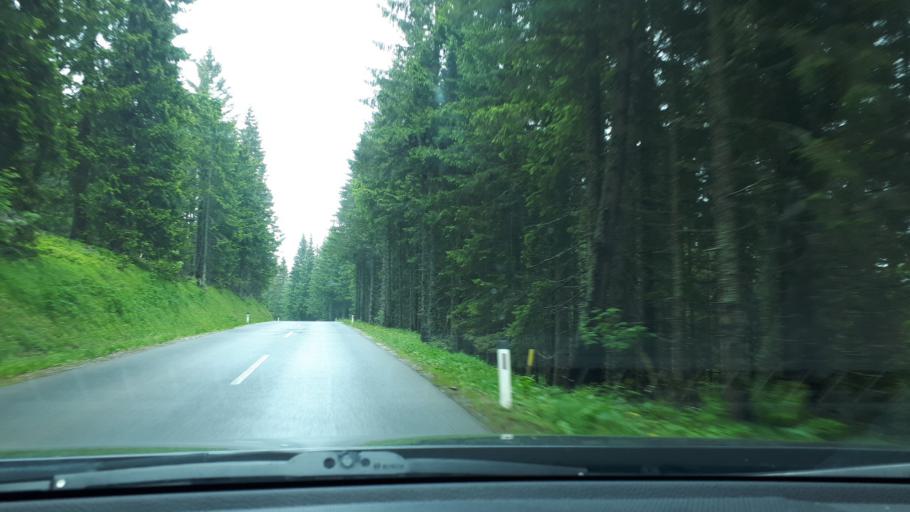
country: AT
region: Styria
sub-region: Politischer Bezirk Voitsberg
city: Modriach
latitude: 46.9193
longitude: 15.0227
